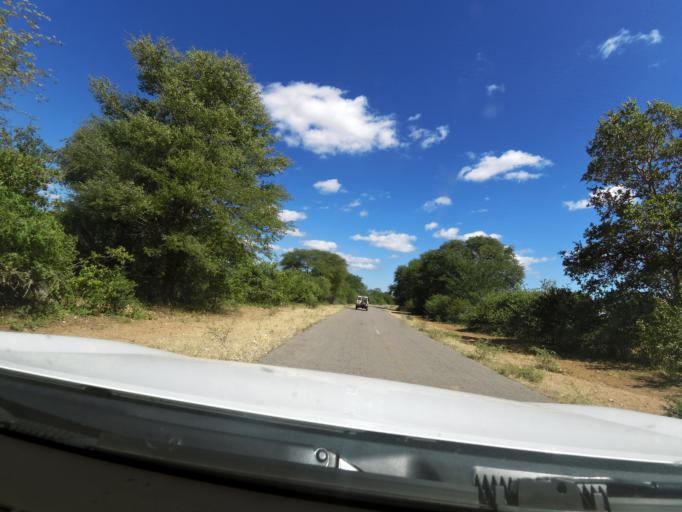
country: ZW
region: Matabeleland North
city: Kamativi Mine
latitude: -18.0057
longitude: 27.1550
